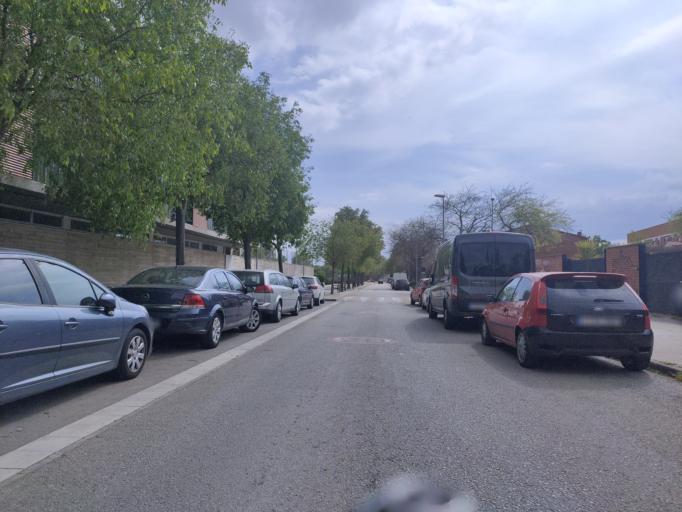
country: ES
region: Catalonia
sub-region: Provincia de Barcelona
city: Mollet del Valles
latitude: 41.5472
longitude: 2.2220
